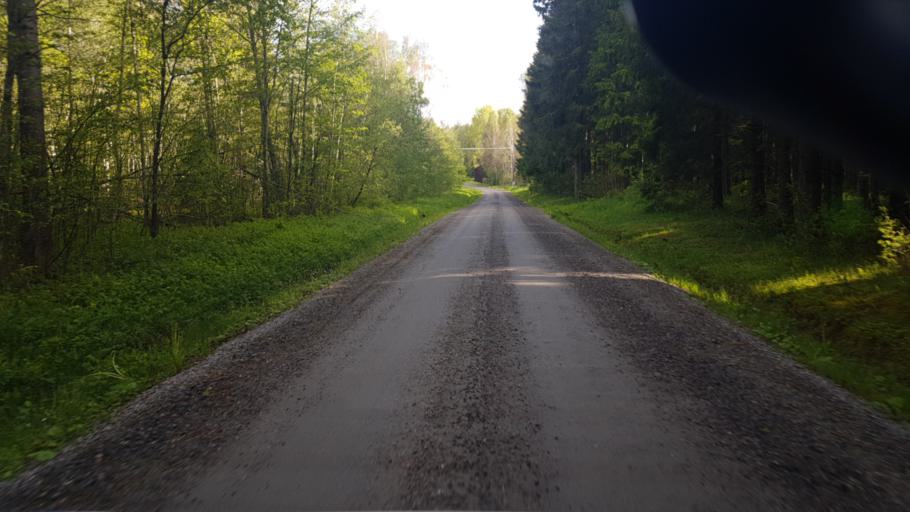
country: SE
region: Vaermland
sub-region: Eda Kommun
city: Amotfors
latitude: 59.7618
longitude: 12.2592
